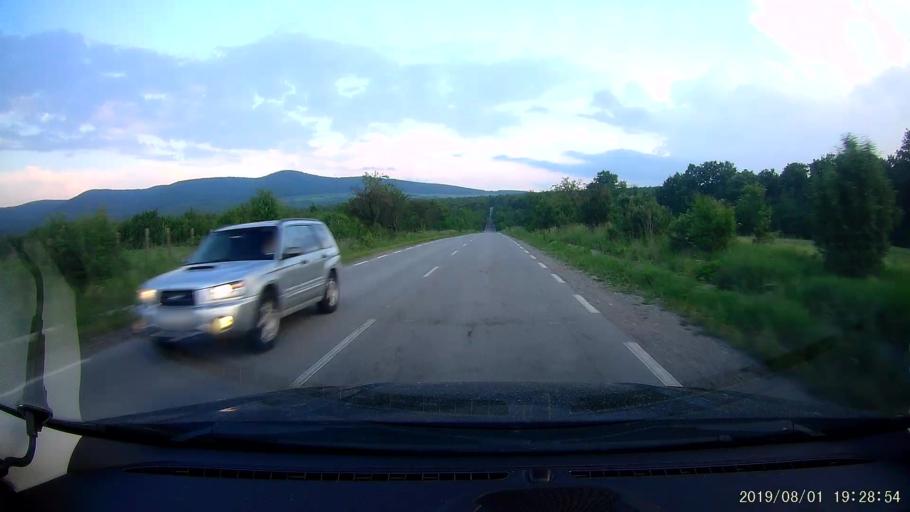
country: BG
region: Burgas
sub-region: Obshtina Sungurlare
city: Sungurlare
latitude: 42.8352
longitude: 26.9124
